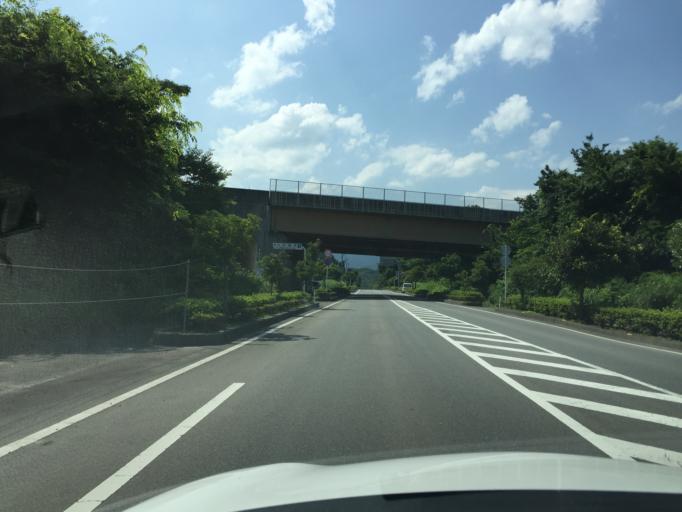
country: JP
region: Ibaraki
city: Kitaibaraki
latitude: 36.9054
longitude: 140.7522
